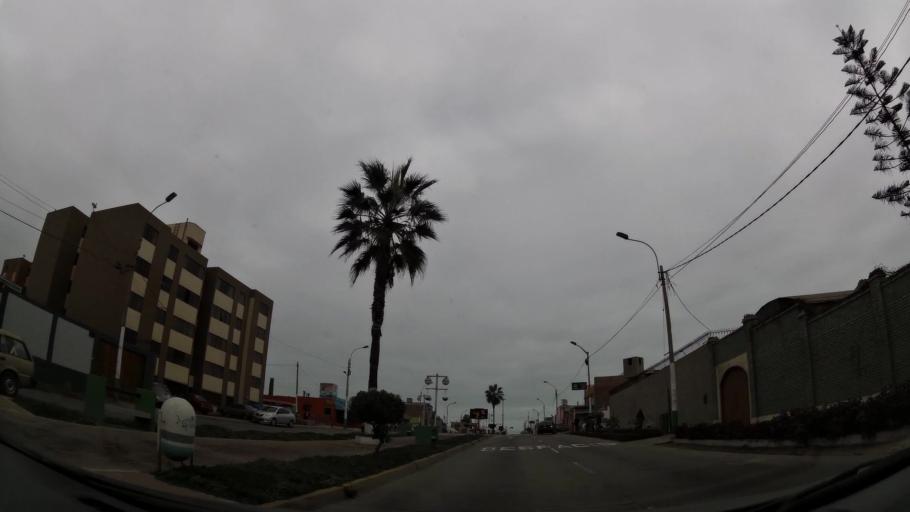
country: PE
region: Callao
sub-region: Callao
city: Callao
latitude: -12.0707
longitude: -77.1223
